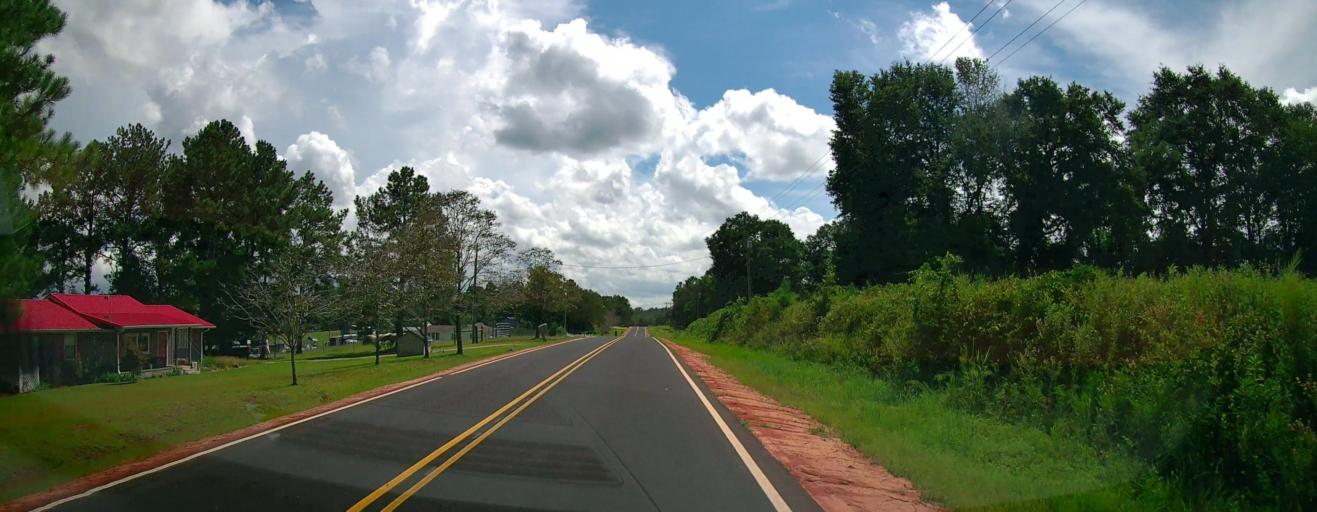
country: US
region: Georgia
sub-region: Peach County
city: Fort Valley
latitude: 32.4875
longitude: -83.8649
